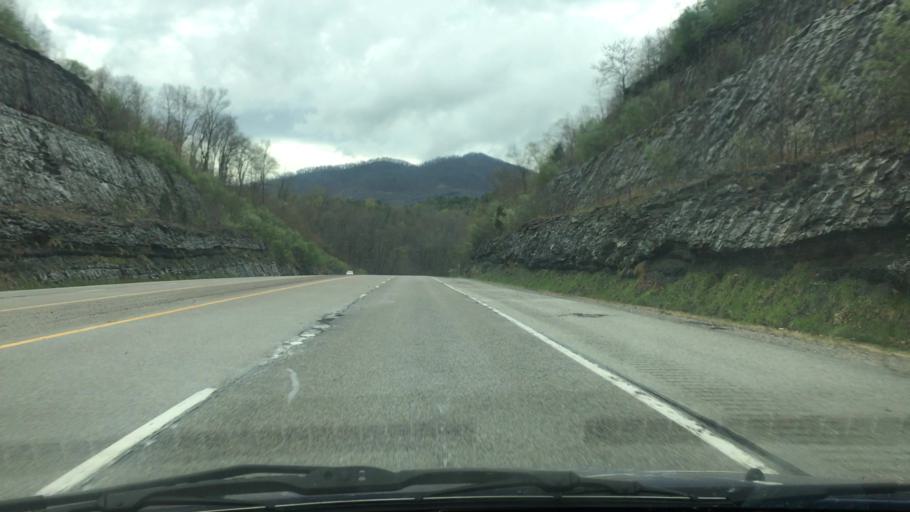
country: US
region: Kentucky
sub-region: Letcher County
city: Jenkins
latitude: 37.1856
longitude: -82.6360
